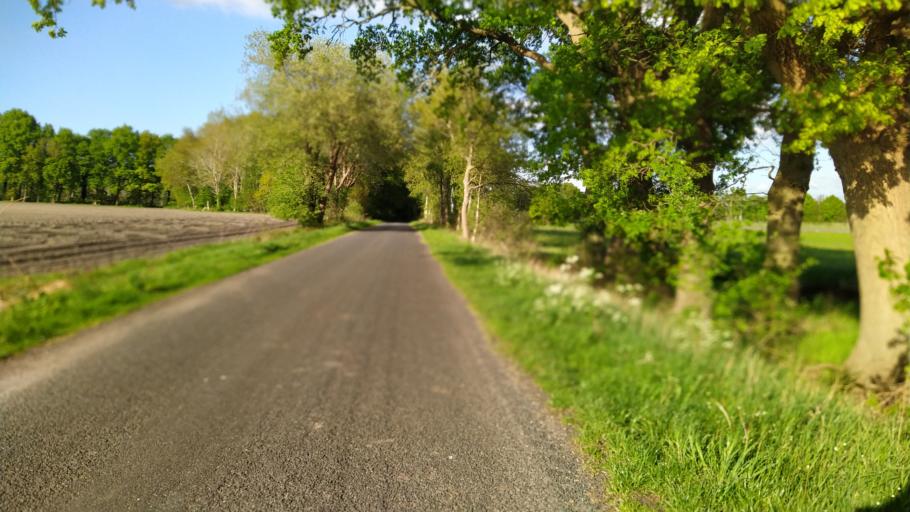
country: DE
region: Lower Saxony
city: Farven
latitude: 53.4256
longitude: 9.3405
